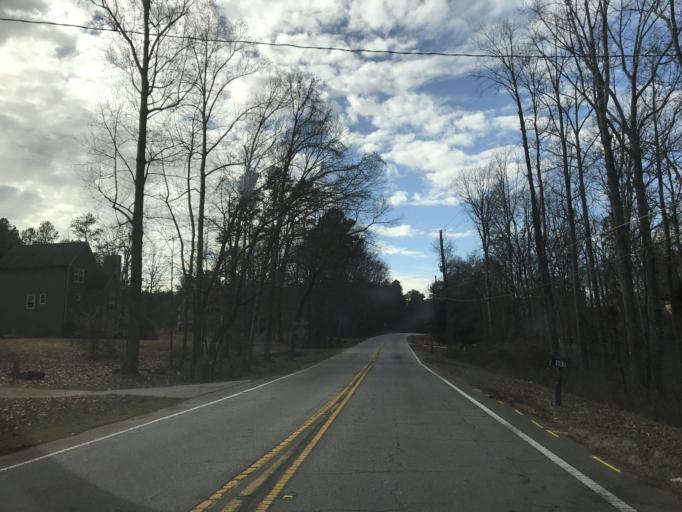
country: US
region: Georgia
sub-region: Douglas County
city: Douglasville
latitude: 33.7987
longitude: -84.7599
